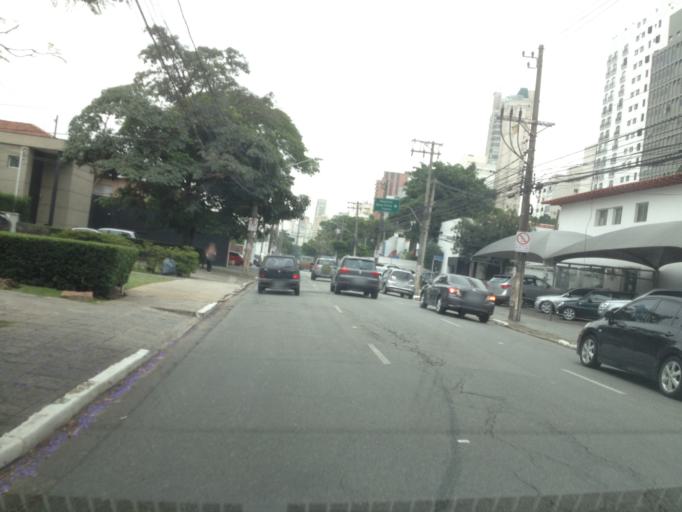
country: BR
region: Sao Paulo
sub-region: Sao Paulo
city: Sao Paulo
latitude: -23.5742
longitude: -46.6605
